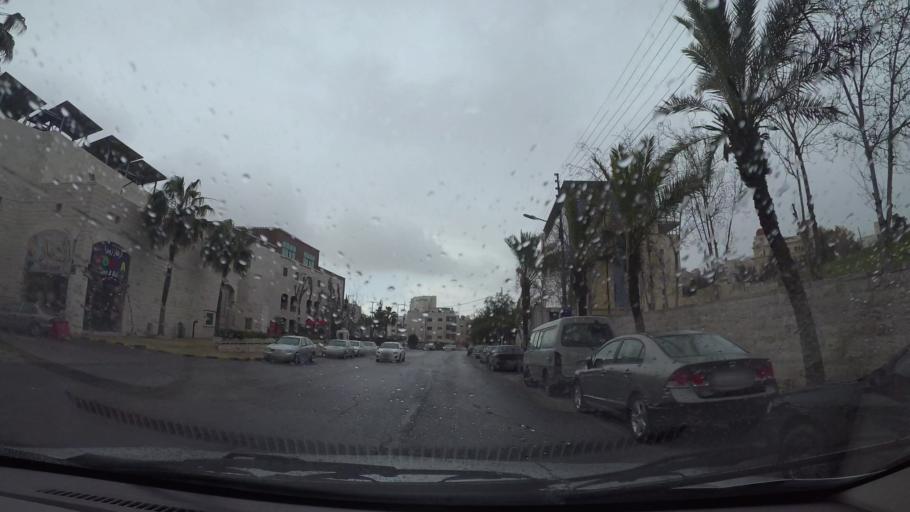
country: JO
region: Amman
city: Al Jubayhah
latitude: 31.9910
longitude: 35.8658
